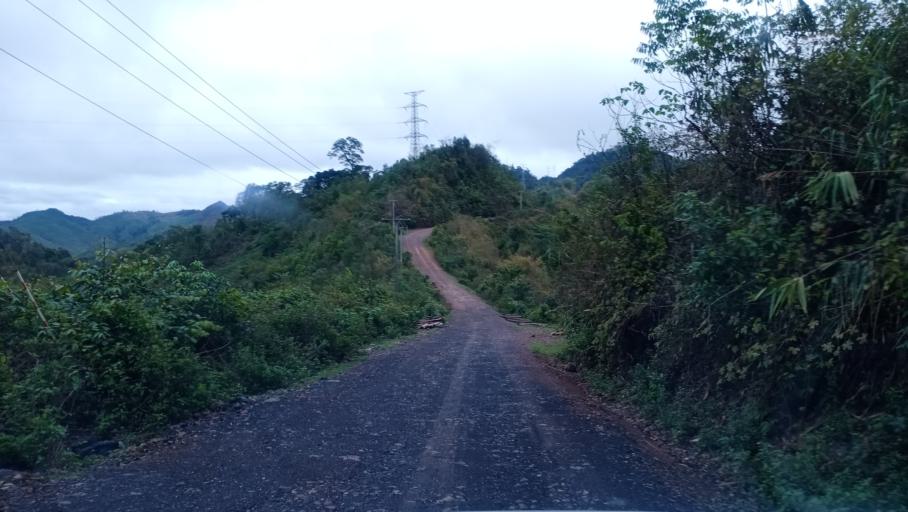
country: LA
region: Phongsali
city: Phongsali
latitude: 21.3401
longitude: 102.0843
